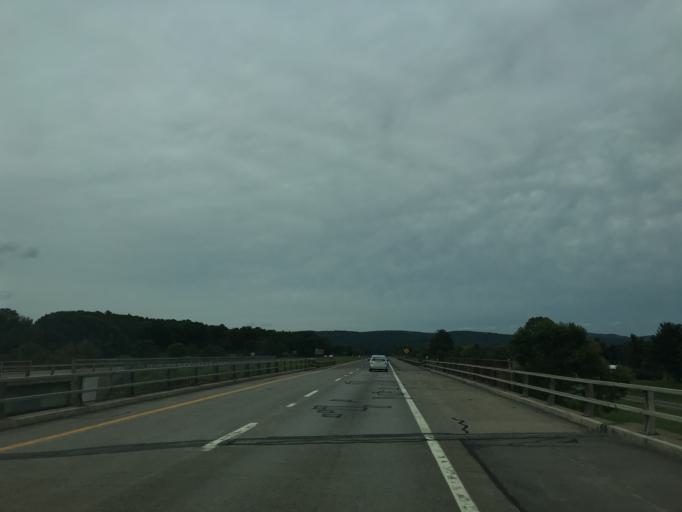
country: US
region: New York
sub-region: Chenango County
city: Bainbridge
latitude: 42.1865
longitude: -75.6381
